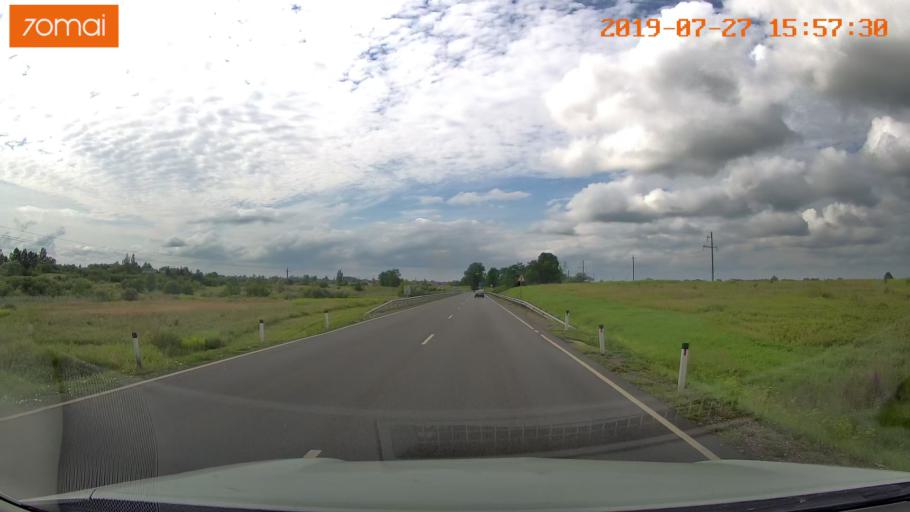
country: RU
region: Kaliningrad
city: Chernyakhovsk
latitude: 54.6239
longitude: 21.8826
